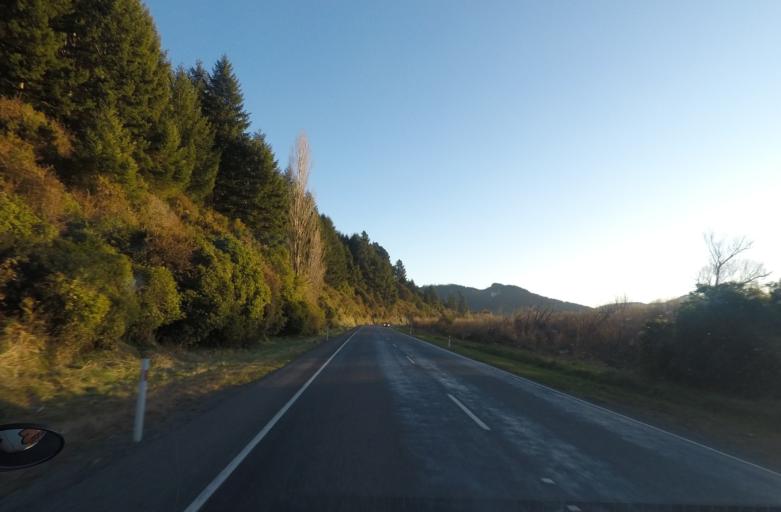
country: NZ
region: Marlborough
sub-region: Marlborough District
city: Picton
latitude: -41.2866
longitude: 173.6880
